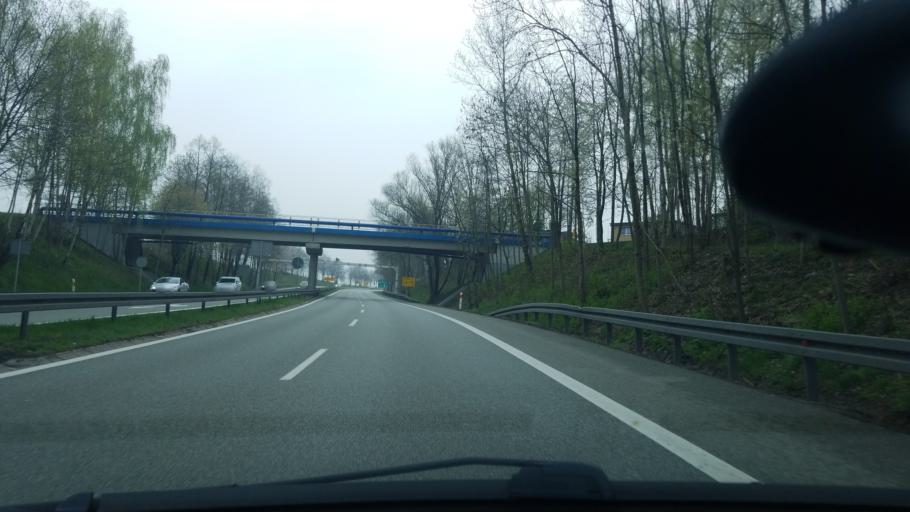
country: PL
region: Silesian Voivodeship
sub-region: Powiat pszczynski
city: Pawlowice
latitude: 49.9662
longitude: 18.7201
